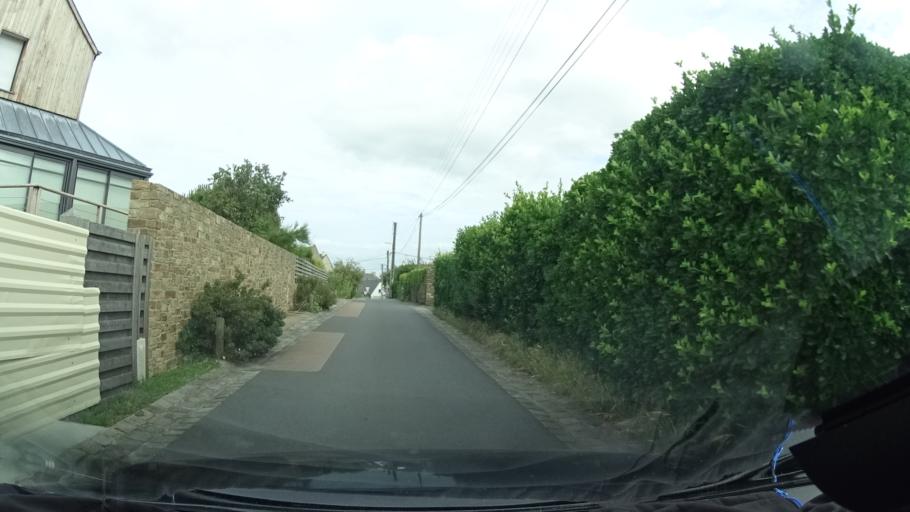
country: FR
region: Brittany
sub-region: Departement d'Ille-et-Vilaine
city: Saint-Malo
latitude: 48.6788
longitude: -1.9843
